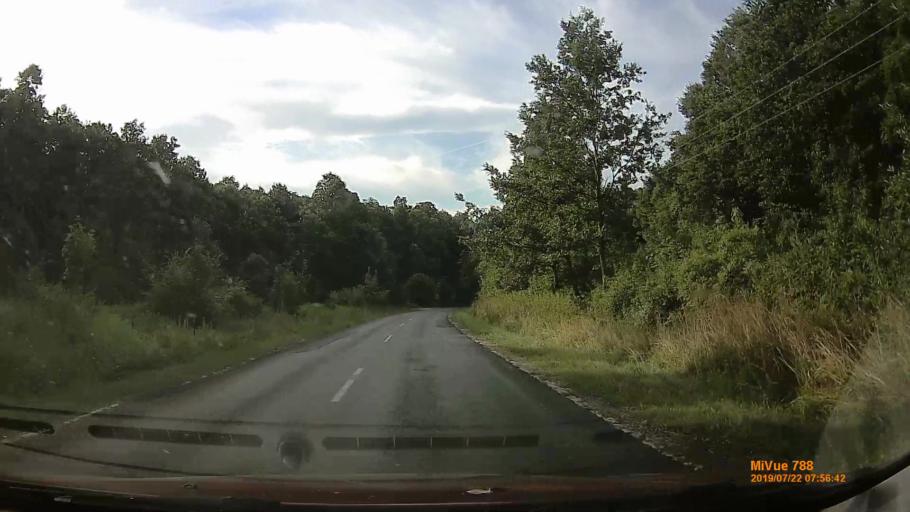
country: HU
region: Veszprem
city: Ajka
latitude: 47.0243
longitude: 17.5732
